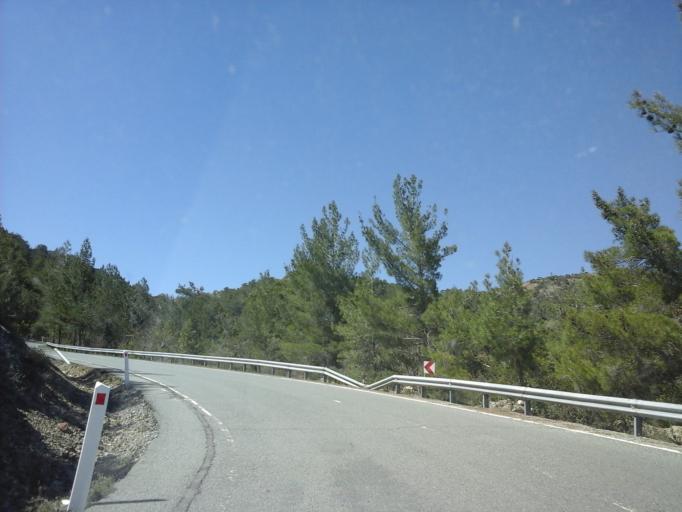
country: CY
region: Lefkosia
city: Kakopetria
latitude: 34.9039
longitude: 32.8607
